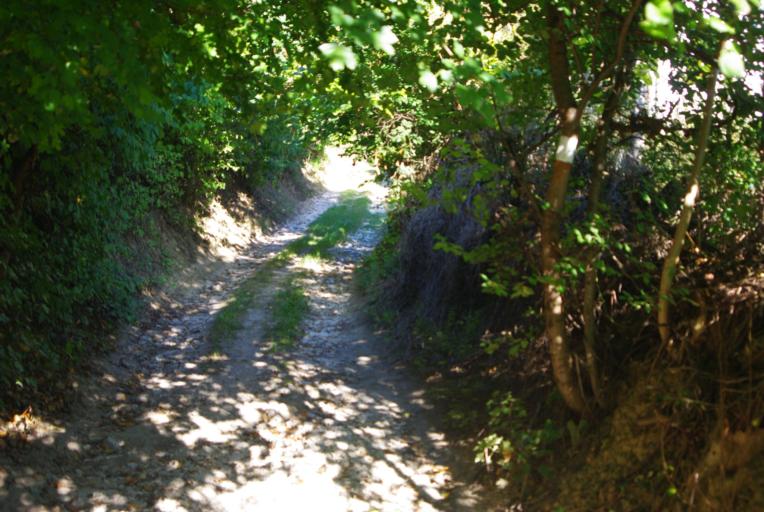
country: HU
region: Pest
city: Zsambek
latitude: 47.5492
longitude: 18.7092
